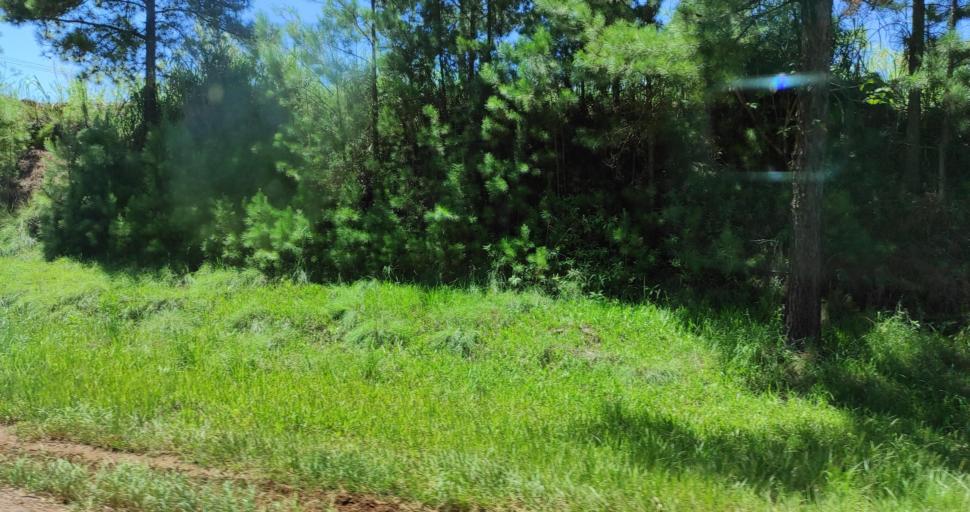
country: AR
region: Misiones
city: Dos de Mayo
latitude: -27.0244
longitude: -54.6575
